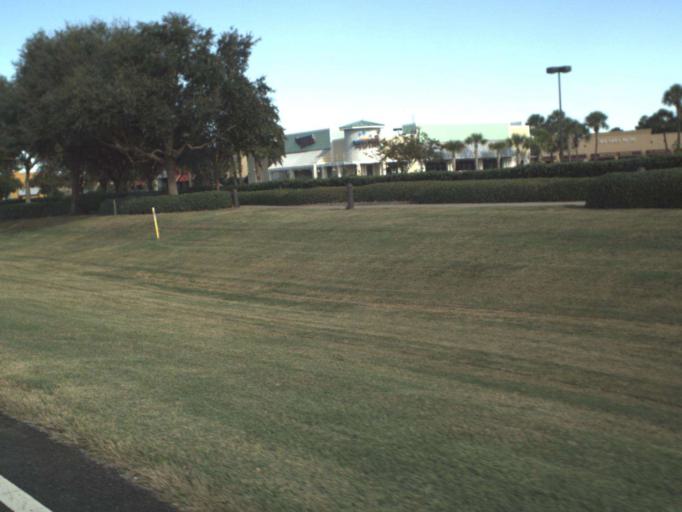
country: US
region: Florida
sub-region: Walton County
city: Miramar Beach
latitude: 30.3772
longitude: -86.3496
